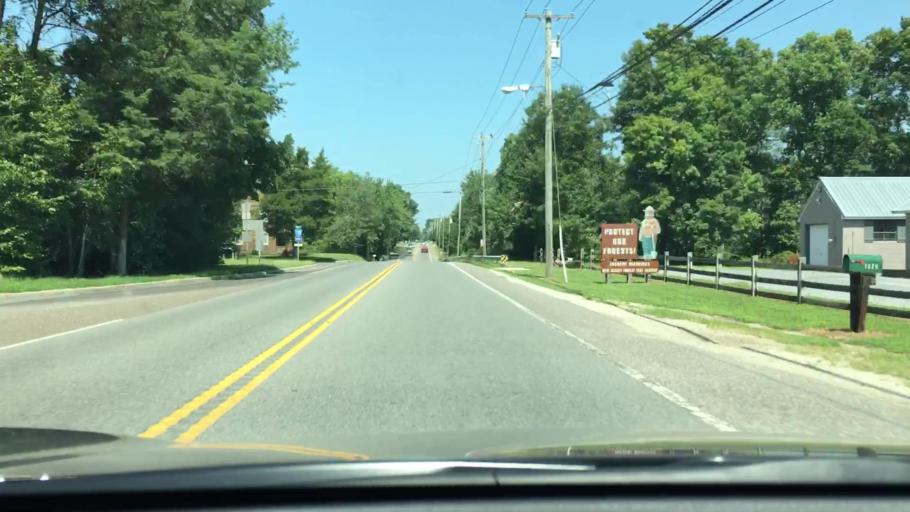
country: US
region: New Jersey
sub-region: Cumberland County
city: Laurel Lake
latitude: 39.3150
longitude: -75.0102
